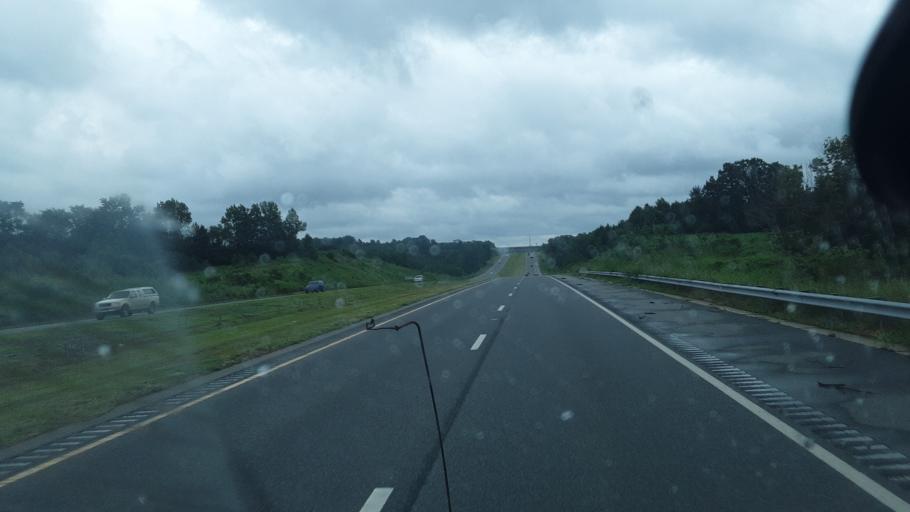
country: US
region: North Carolina
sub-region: Randolph County
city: Randleman
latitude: 35.8031
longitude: -79.8445
